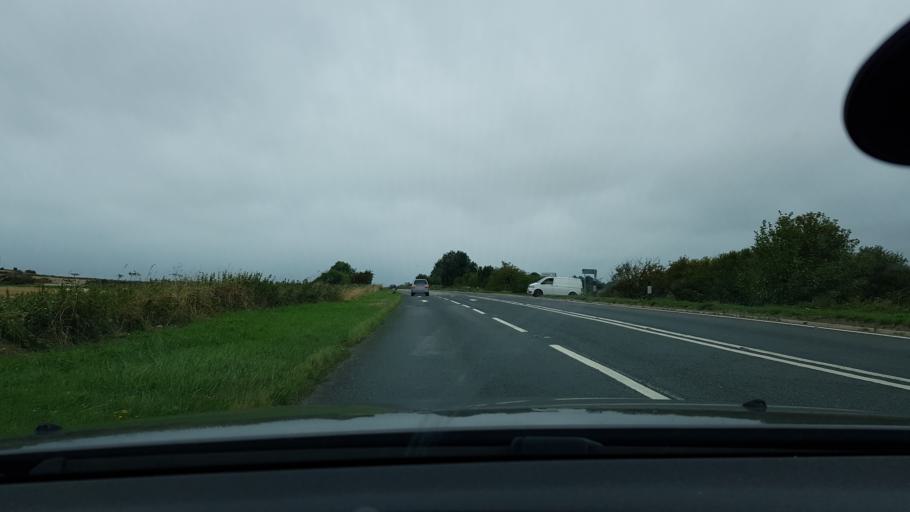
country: GB
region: England
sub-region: Wiltshire
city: Avebury
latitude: 51.4306
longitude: -1.9186
